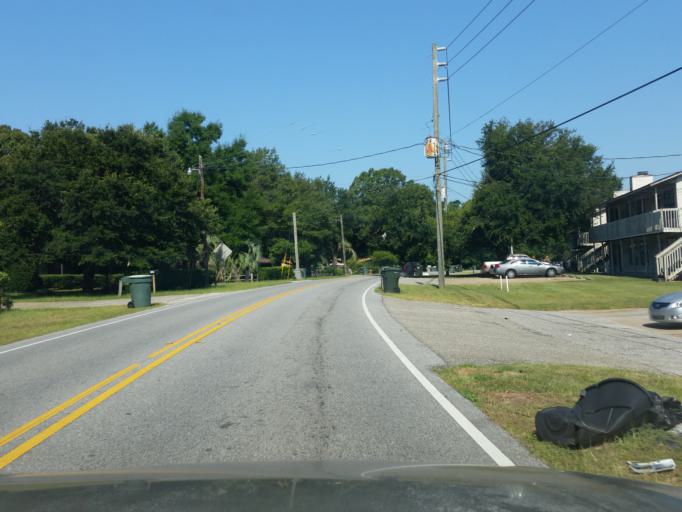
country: US
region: Florida
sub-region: Escambia County
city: Ferry Pass
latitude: 30.5172
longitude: -87.2274
